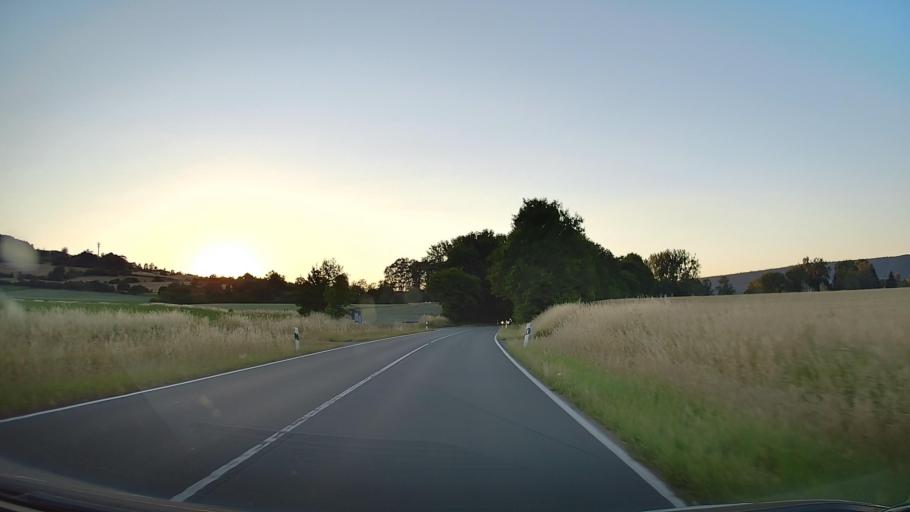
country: DE
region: North Rhine-Westphalia
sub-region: Regierungsbezirk Detmold
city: Lugde
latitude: 51.9723
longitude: 9.2333
